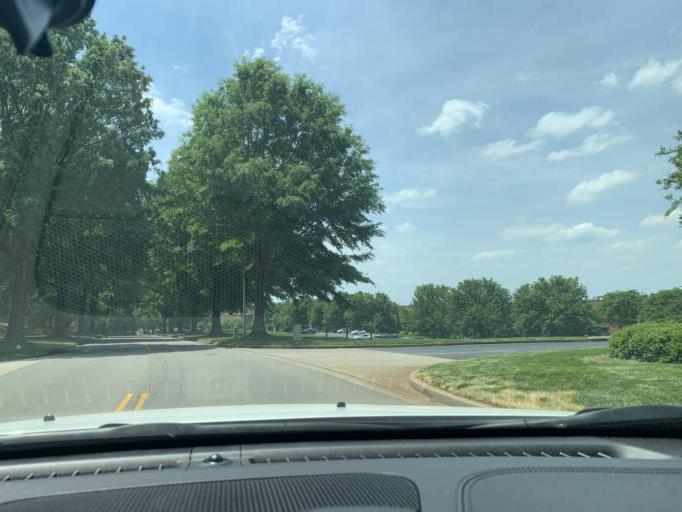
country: US
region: Georgia
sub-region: Fulton County
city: Johns Creek
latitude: 34.1135
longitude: -84.1966
